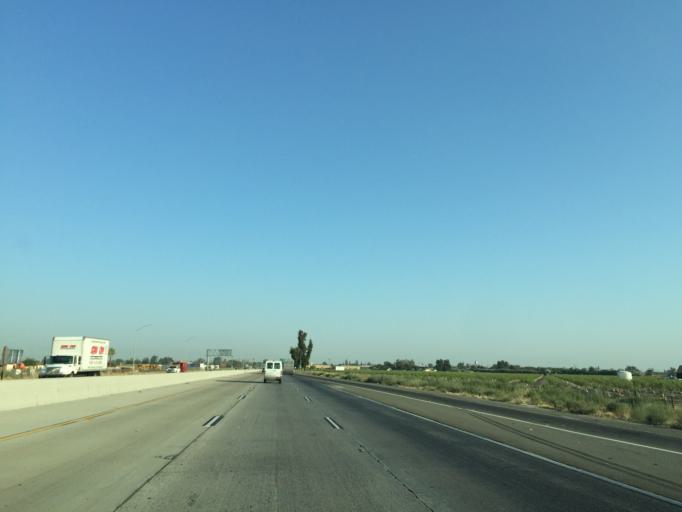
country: US
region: California
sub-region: Fresno County
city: Selma
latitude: 36.5484
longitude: -119.5977
